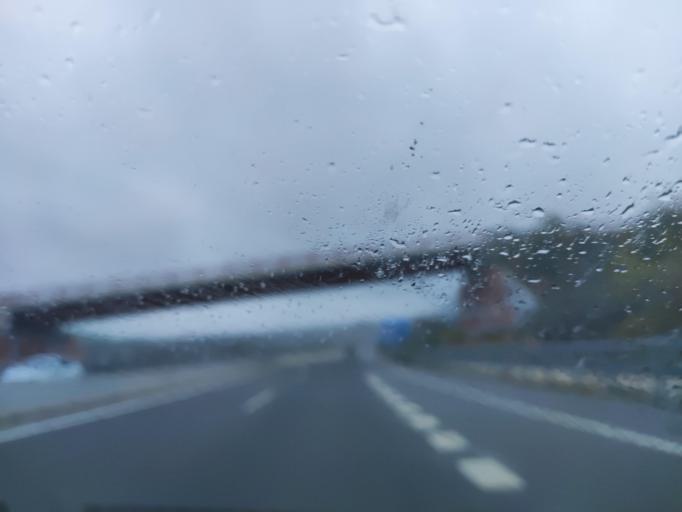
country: ES
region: Castille-La Mancha
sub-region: Province of Toledo
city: Toledo
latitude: 39.8717
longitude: -4.0784
